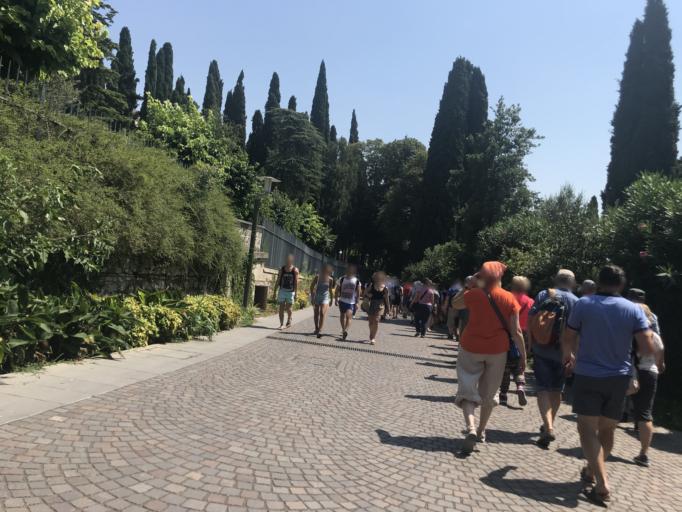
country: IT
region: Lombardy
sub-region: Provincia di Brescia
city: Sirmione
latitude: 45.4963
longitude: 10.6057
